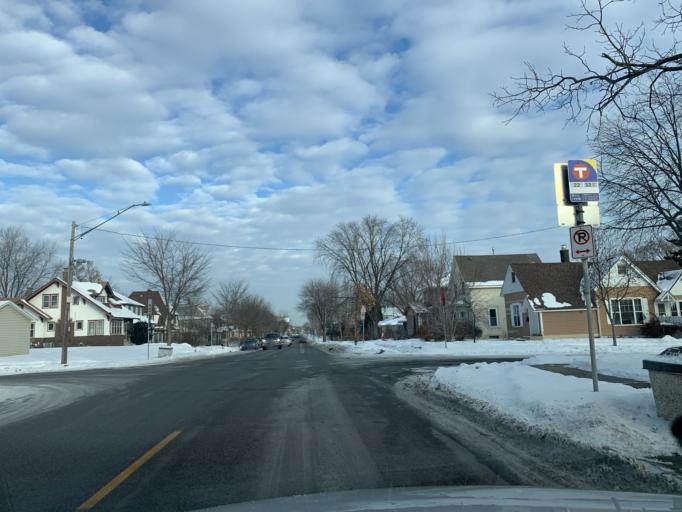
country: US
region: Minnesota
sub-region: Anoka County
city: Columbia Heights
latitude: 45.0255
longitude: -93.2880
